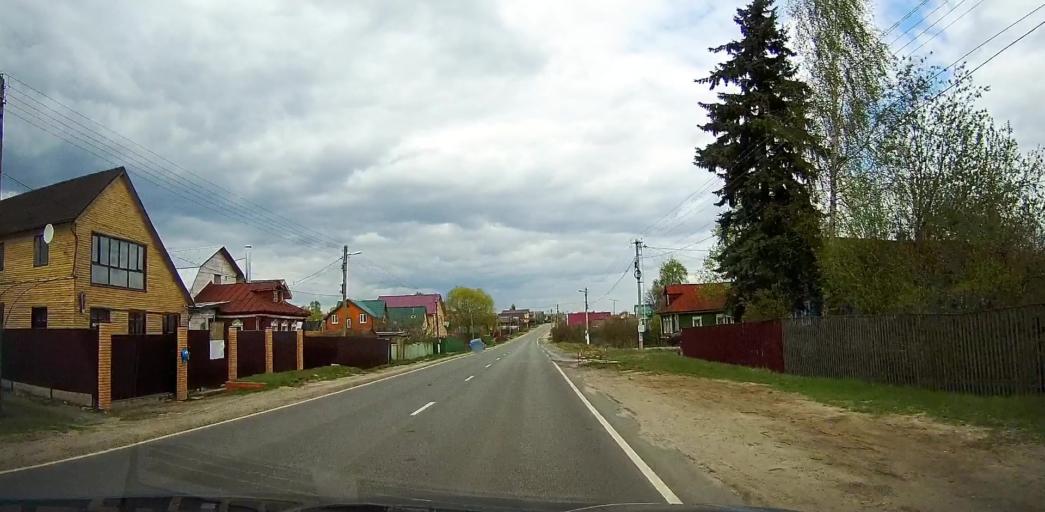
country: RU
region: Moskovskaya
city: Ashitkovo
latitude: 55.4500
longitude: 38.5931
